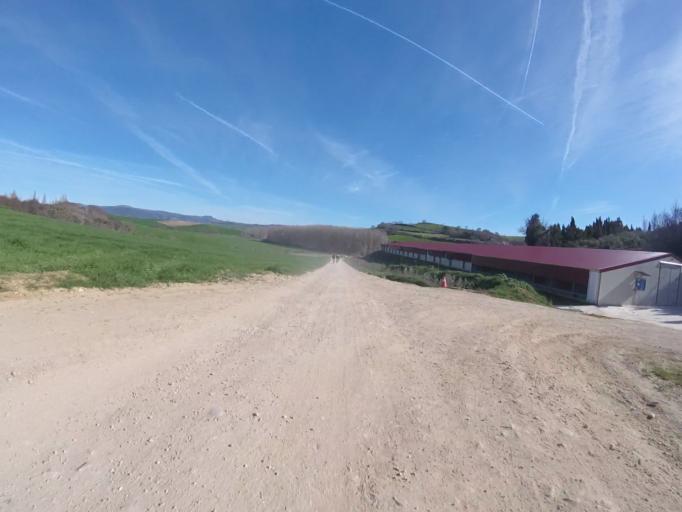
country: ES
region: Navarre
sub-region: Provincia de Navarra
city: Villatuerta
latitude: 42.6910
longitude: -1.9943
